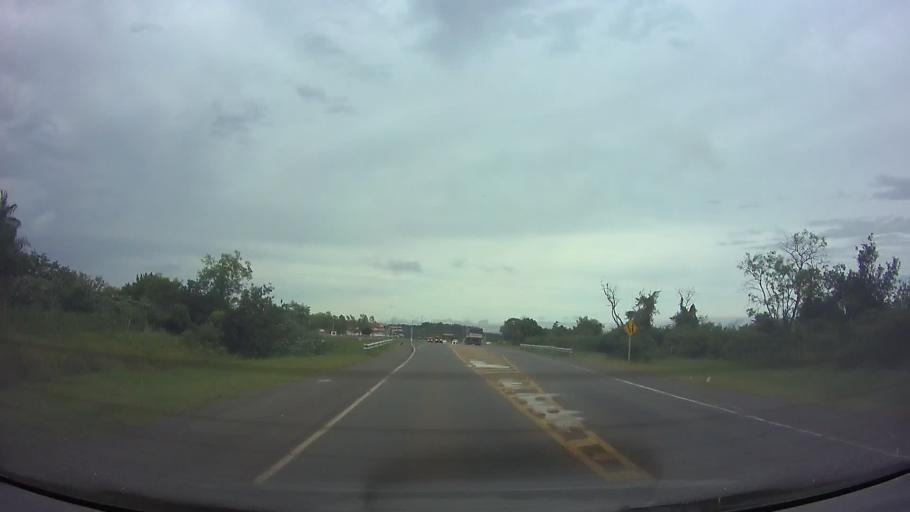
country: PY
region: Paraguari
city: Carapegua
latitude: -25.7652
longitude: -57.2331
